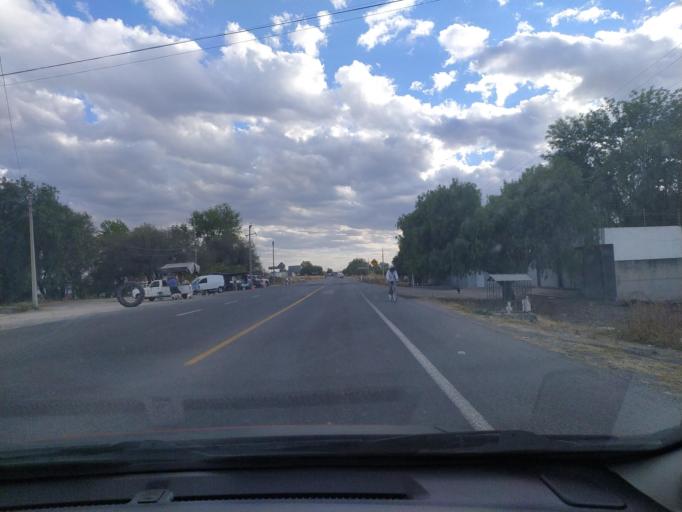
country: LA
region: Oudomxai
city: Muang La
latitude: 21.0211
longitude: 101.8264
